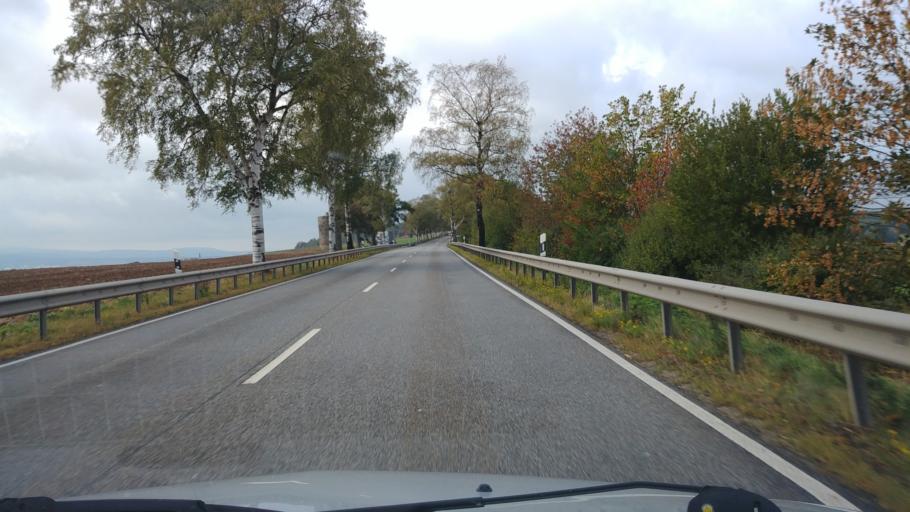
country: DE
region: Rheinland-Pfalz
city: Kleinich
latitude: 49.8579
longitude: 7.1720
